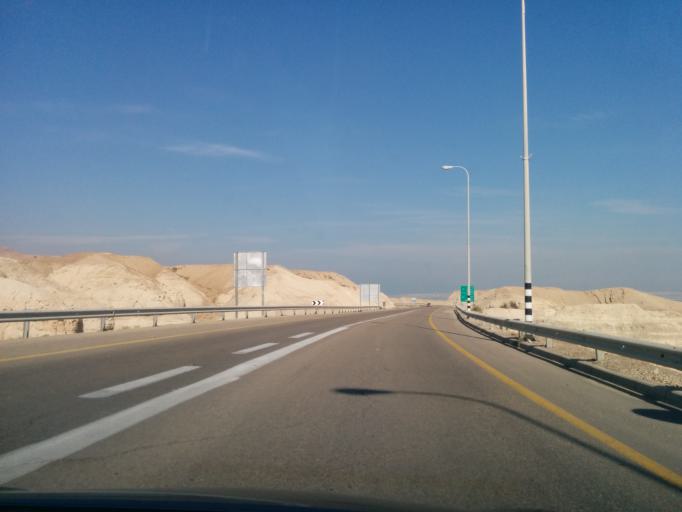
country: IL
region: Southern District
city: `En Boqeq
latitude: 31.1422
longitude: 35.3603
